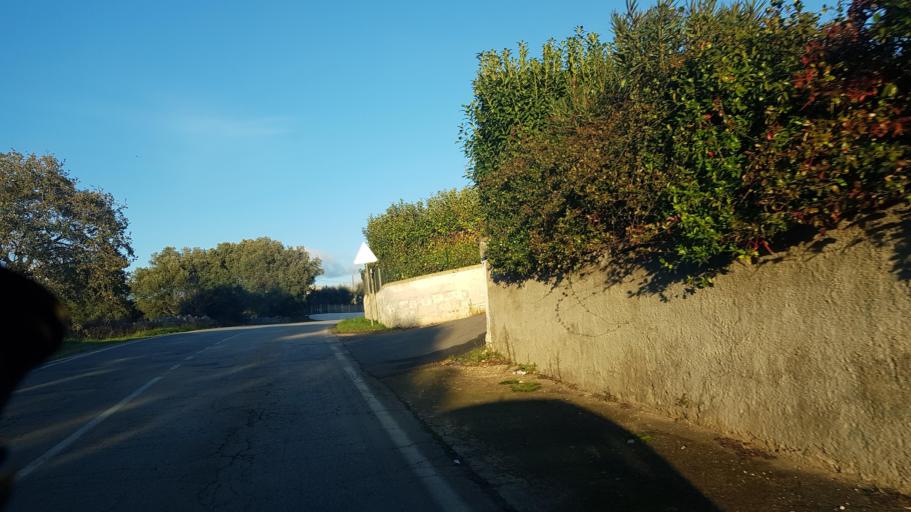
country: IT
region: Apulia
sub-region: Provincia di Brindisi
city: Ostuni
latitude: 40.7130
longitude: 17.5540
